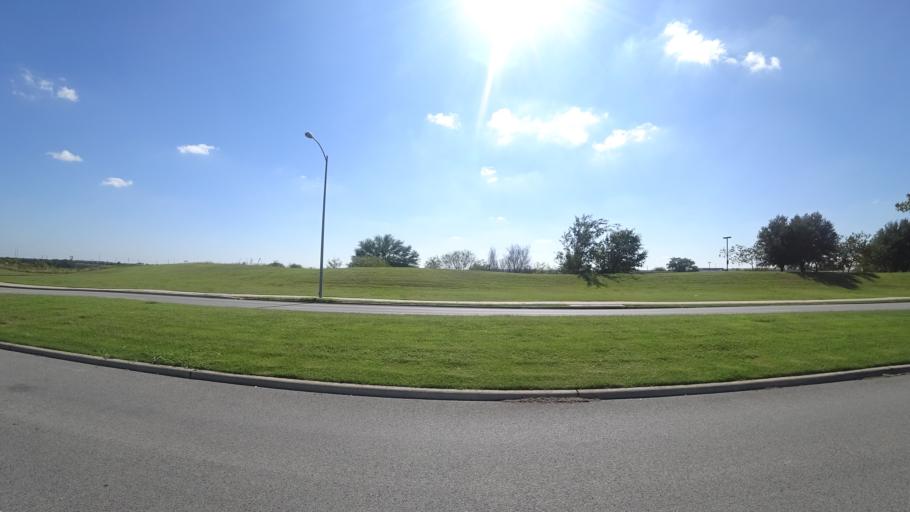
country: US
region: Texas
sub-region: Travis County
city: Manor
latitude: 30.3390
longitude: -97.6107
